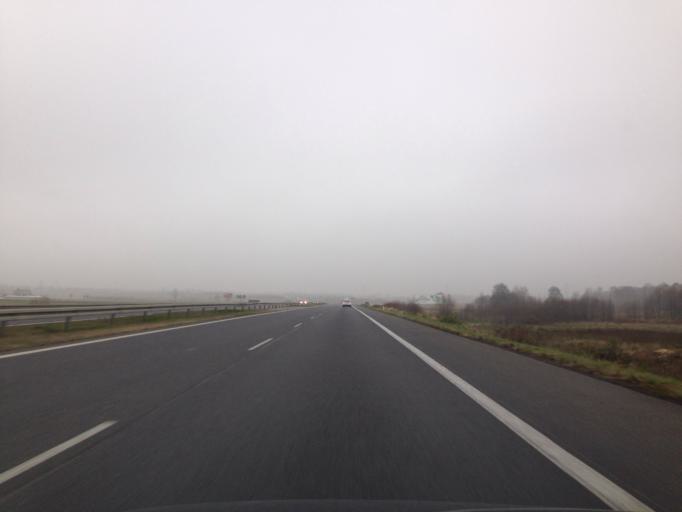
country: PL
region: Lodz Voivodeship
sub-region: Powiat radomszczanski
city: Kamiensk
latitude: 51.2203
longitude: 19.4977
